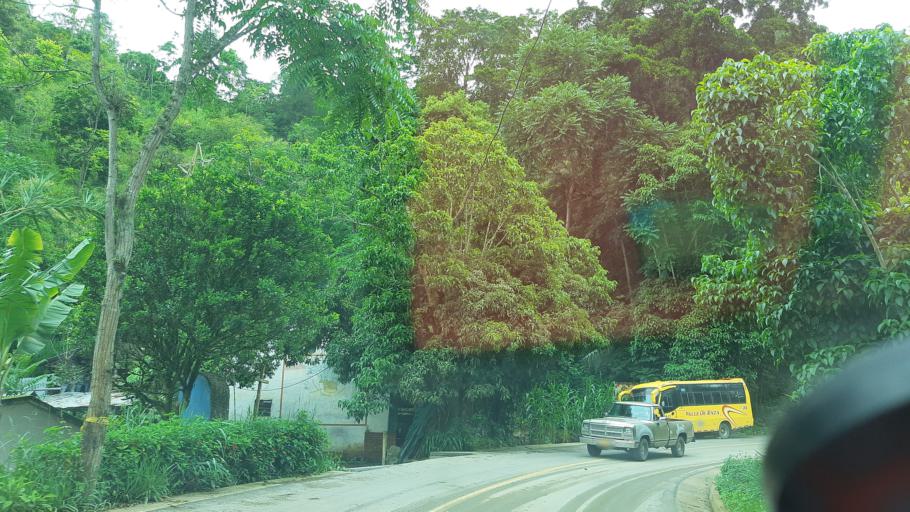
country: CO
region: Cundinamarca
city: Tenza
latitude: 5.0735
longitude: -73.4061
